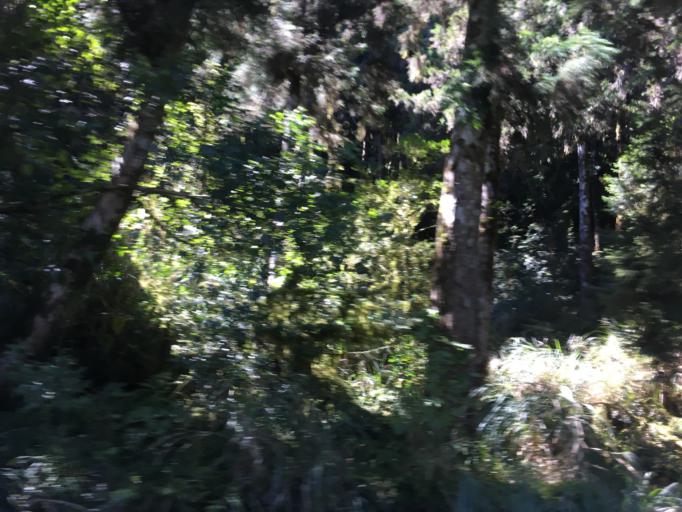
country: TW
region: Taiwan
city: Daxi
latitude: 24.5739
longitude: 121.4179
